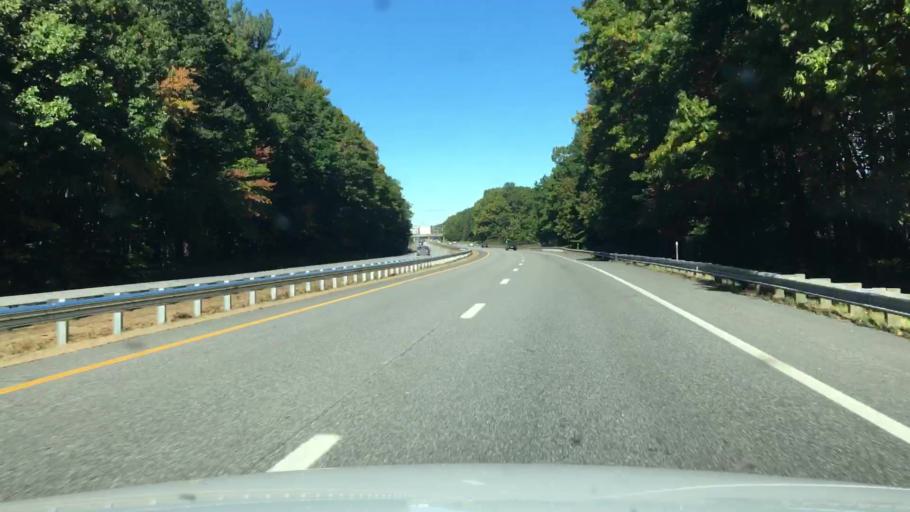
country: US
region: New Hampshire
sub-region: Strafford County
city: Dover
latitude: 43.1579
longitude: -70.8489
